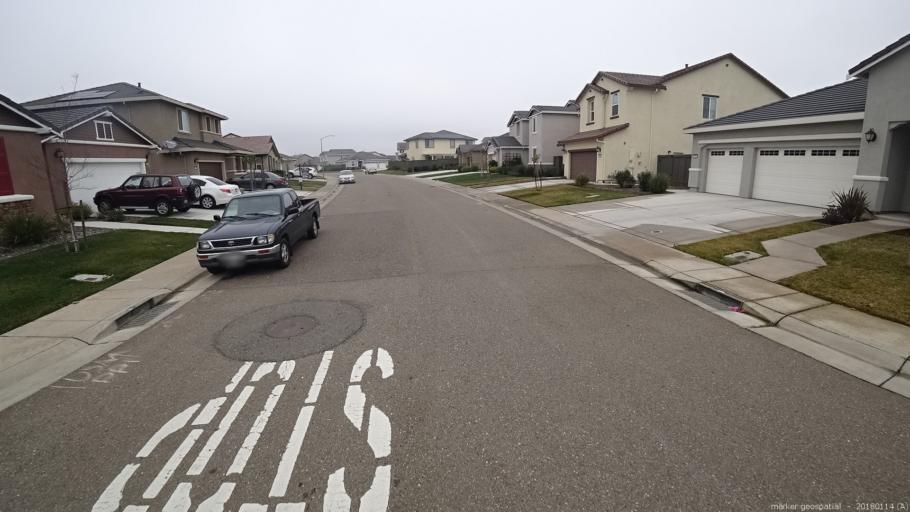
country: US
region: California
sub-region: Sacramento County
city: Rancho Cordova
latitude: 38.5294
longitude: -121.2257
